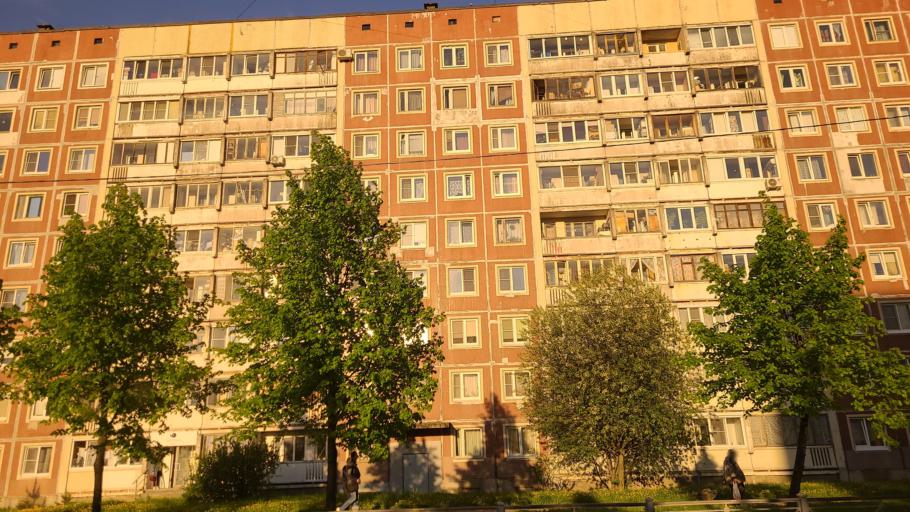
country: RU
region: St.-Petersburg
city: Kolpino
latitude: 59.7372
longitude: 30.5798
